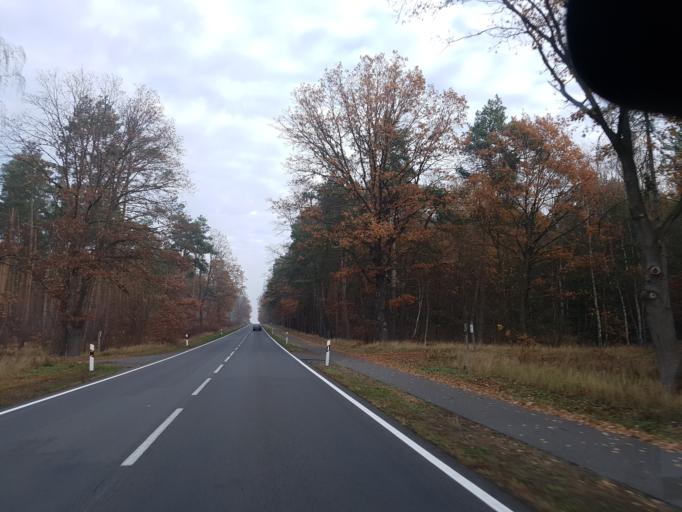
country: DE
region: Saxony-Anhalt
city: Kropstadt
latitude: 51.9821
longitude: 12.7630
